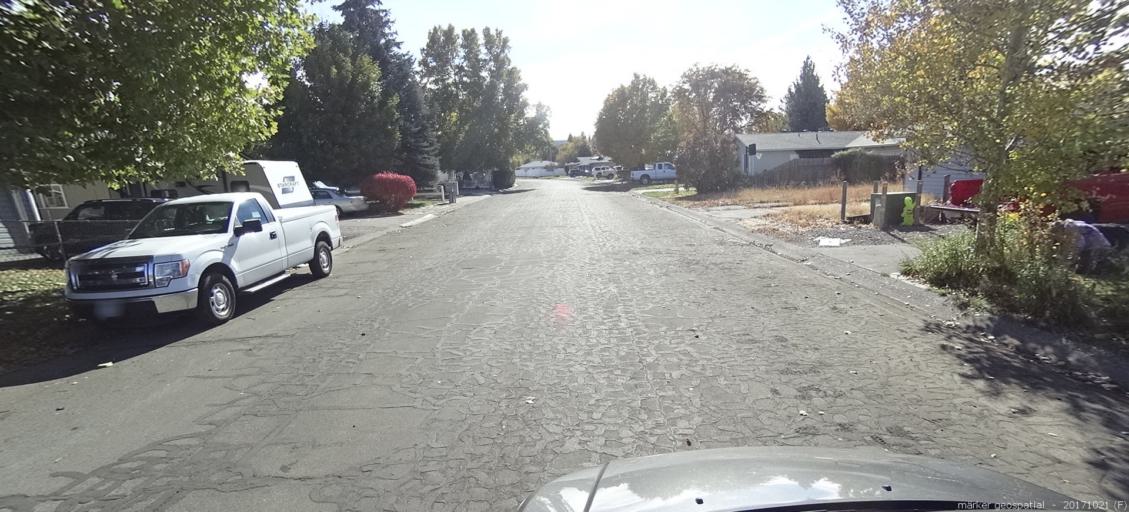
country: US
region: California
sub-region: Shasta County
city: Burney
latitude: 40.8860
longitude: -121.6619
